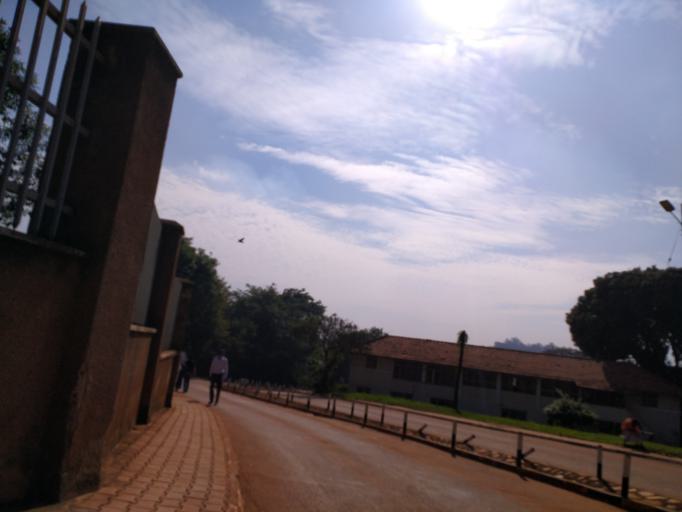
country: UG
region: Central Region
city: Kampala Central Division
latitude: 0.3365
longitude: 32.5686
